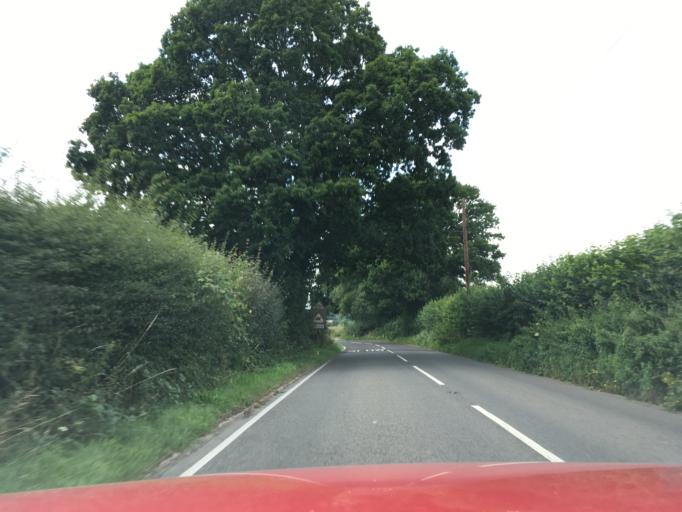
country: GB
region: England
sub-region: East Sussex
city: Crowborough
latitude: 51.1120
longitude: 0.1646
